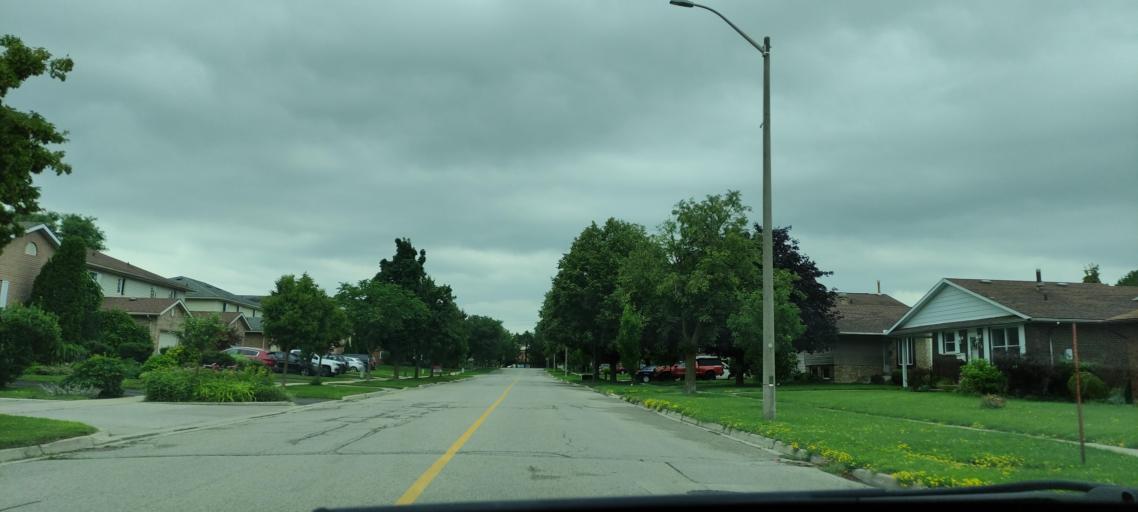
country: CA
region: Ontario
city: Stratford
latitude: 43.3833
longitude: -80.9754
